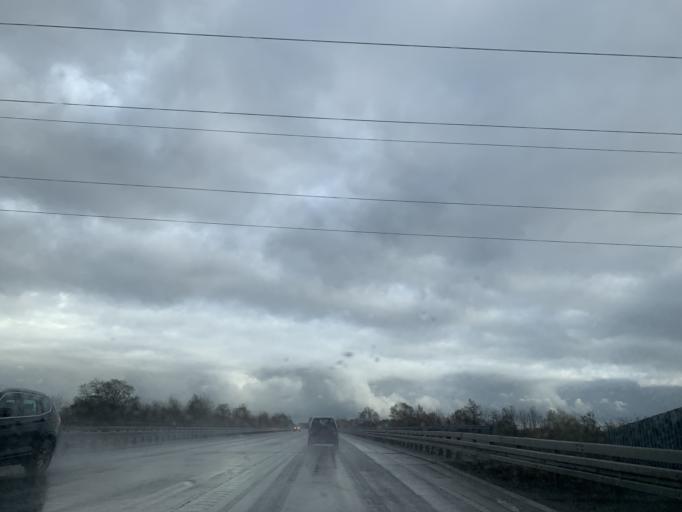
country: DE
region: North Rhine-Westphalia
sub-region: Regierungsbezirk Munster
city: Gronau
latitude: 52.1949
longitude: 7.0170
